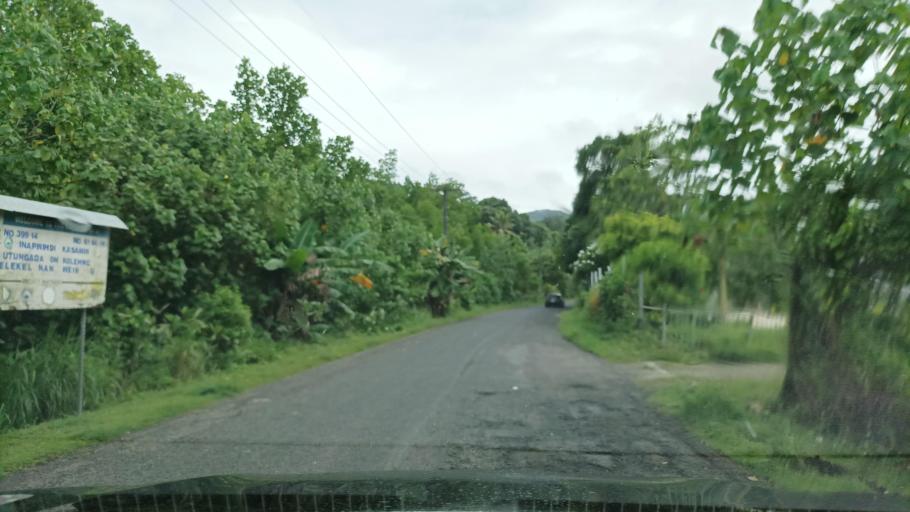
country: FM
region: Pohnpei
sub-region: Kolonia Municipality
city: Kolonia
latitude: 6.9238
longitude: 158.2861
